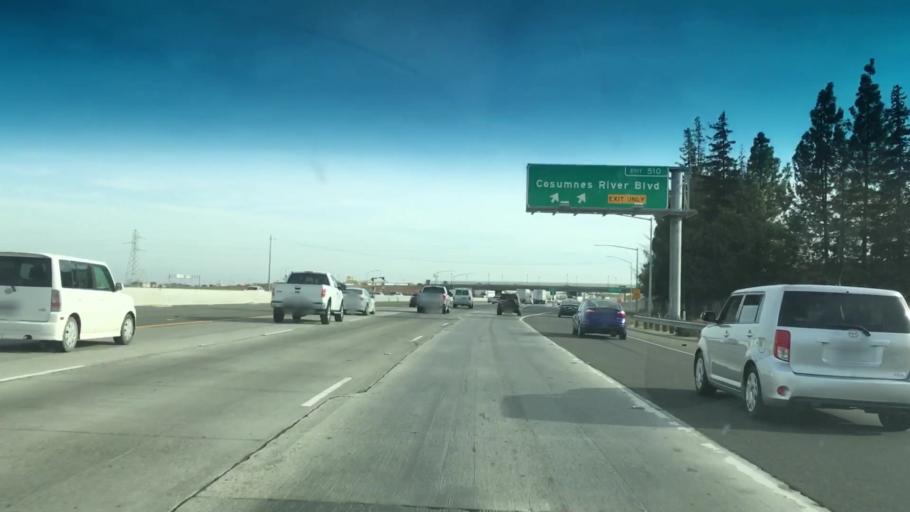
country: US
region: California
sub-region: Sacramento County
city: Parkway
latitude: 38.4708
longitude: -121.4996
